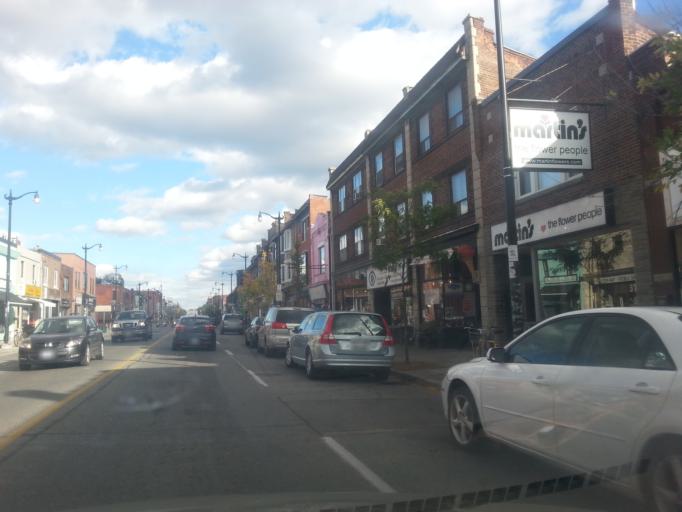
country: CA
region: Ontario
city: Toronto
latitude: 43.6655
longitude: -79.4733
